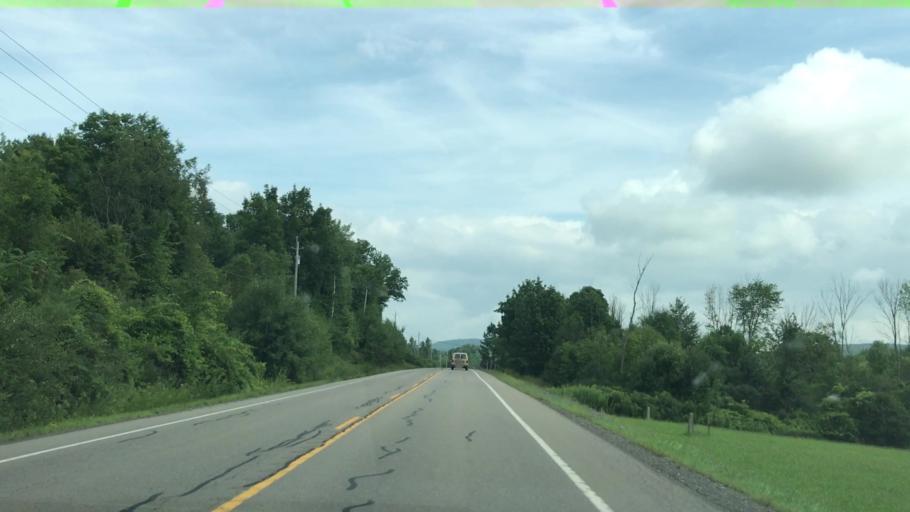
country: US
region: New York
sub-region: Steuben County
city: Bath
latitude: 42.4749
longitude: -77.2953
